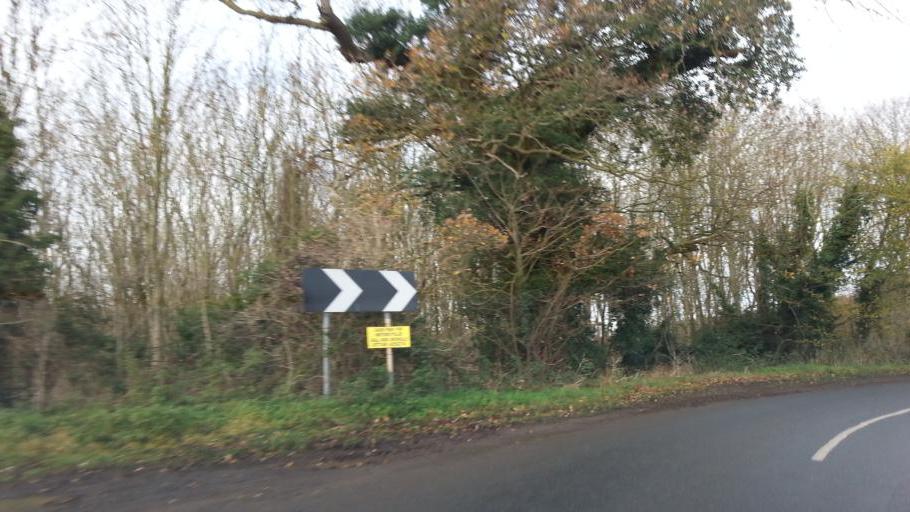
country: GB
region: England
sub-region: Suffolk
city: Wickham Market
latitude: 52.1471
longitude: 1.4307
